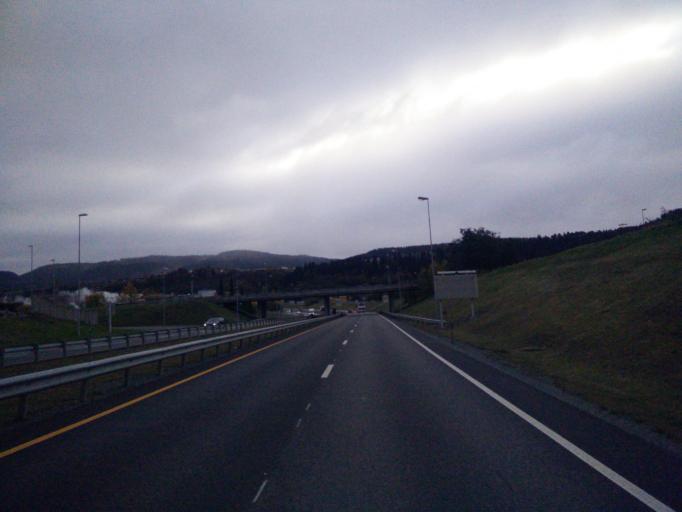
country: NO
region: Sor-Trondelag
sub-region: Trondheim
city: Trondheim
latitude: 63.4255
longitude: 10.5159
